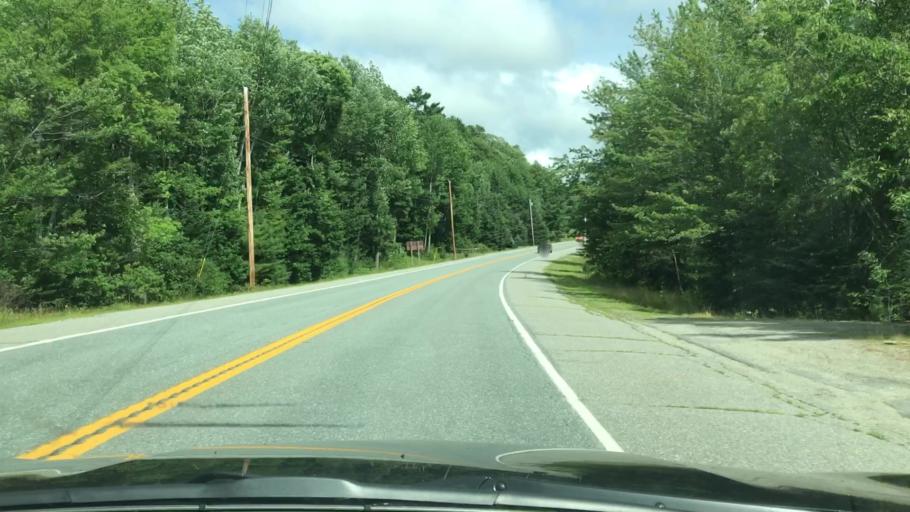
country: US
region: Maine
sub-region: Hancock County
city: Orland
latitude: 44.5675
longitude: -68.6752
